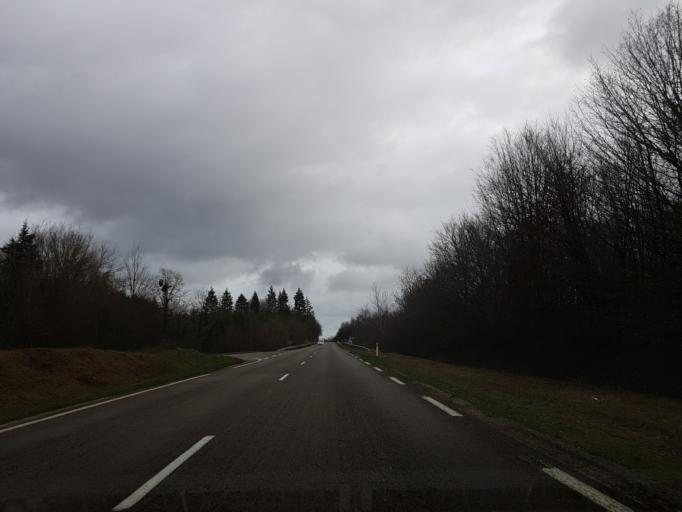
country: FR
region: Franche-Comte
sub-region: Departement de la Haute-Saone
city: Scey-sur-Saone-et-Saint-Albin
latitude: 47.6983
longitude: 5.9560
